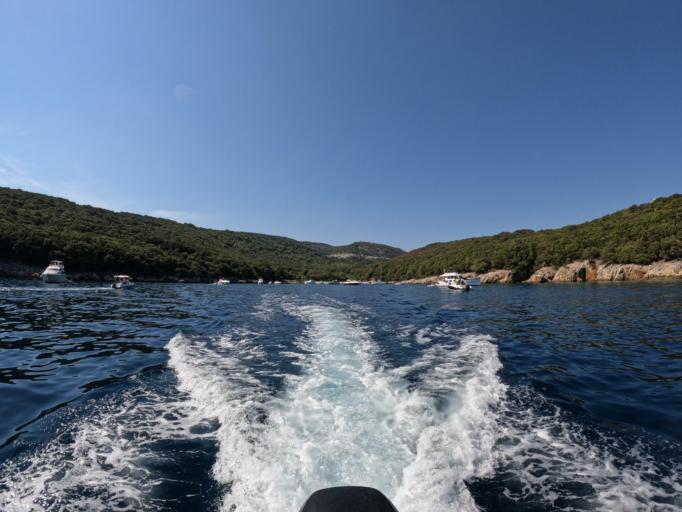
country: HR
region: Primorsko-Goranska
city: Cres
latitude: 44.9499
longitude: 14.4638
